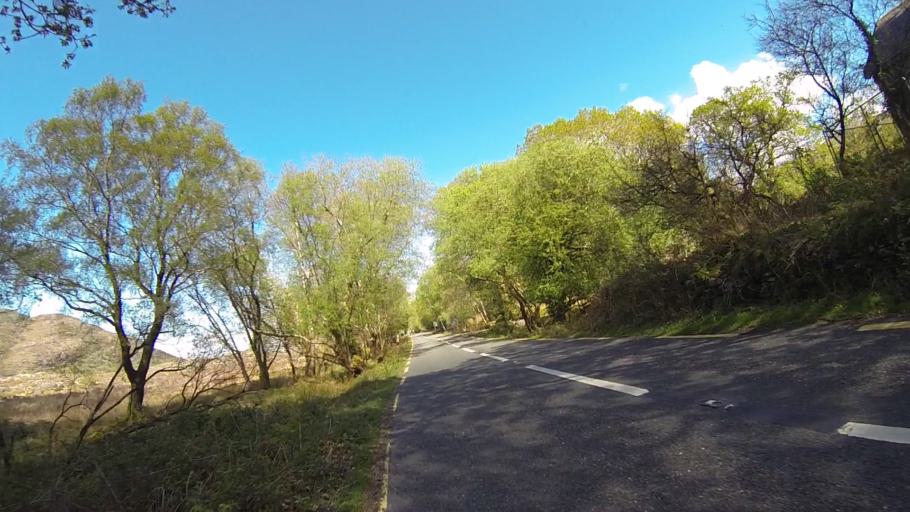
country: IE
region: Munster
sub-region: Ciarrai
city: Cill Airne
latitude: 51.9875
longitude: -9.5587
